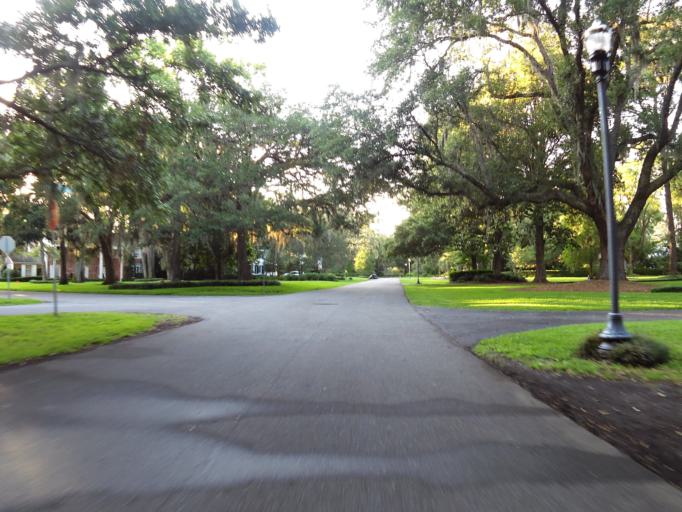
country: US
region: Florida
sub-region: Duval County
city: Jacksonville
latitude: 30.2583
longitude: -81.6964
